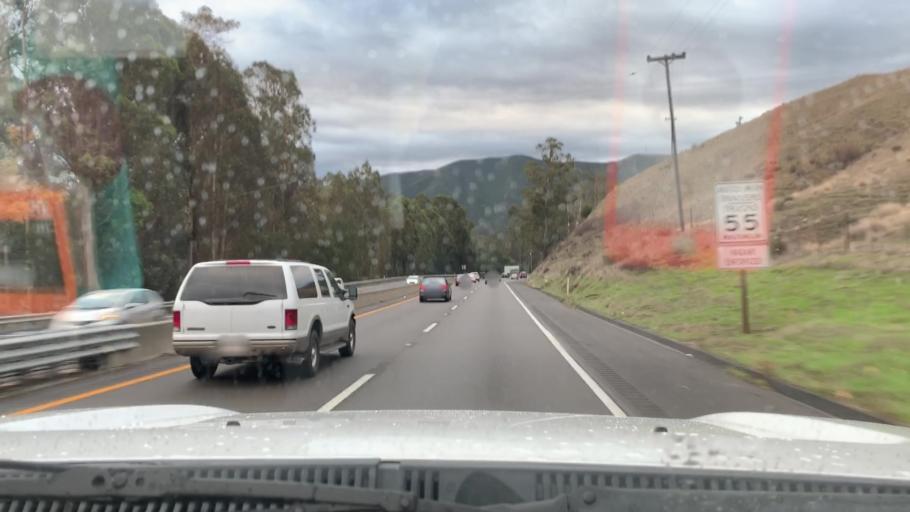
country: US
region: California
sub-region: San Luis Obispo County
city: San Luis Obispo
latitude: 35.3025
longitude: -120.6259
